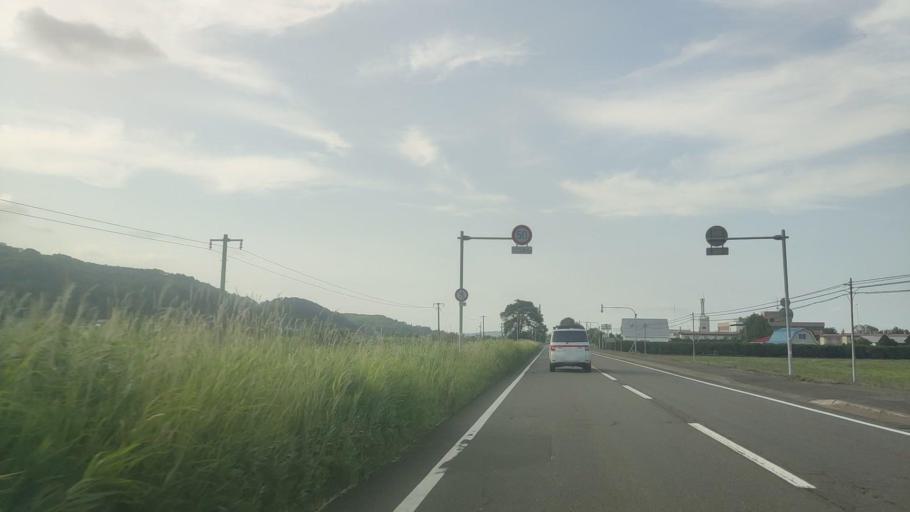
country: JP
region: Hokkaido
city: Iwamizawa
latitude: 42.9961
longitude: 141.7899
